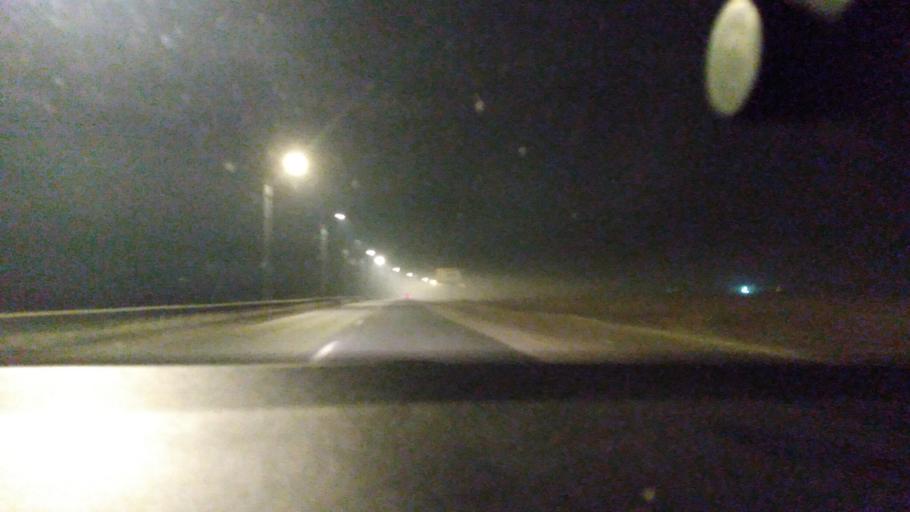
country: RU
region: Moskovskaya
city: Yegor'yevsk
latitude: 55.3984
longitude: 39.0630
